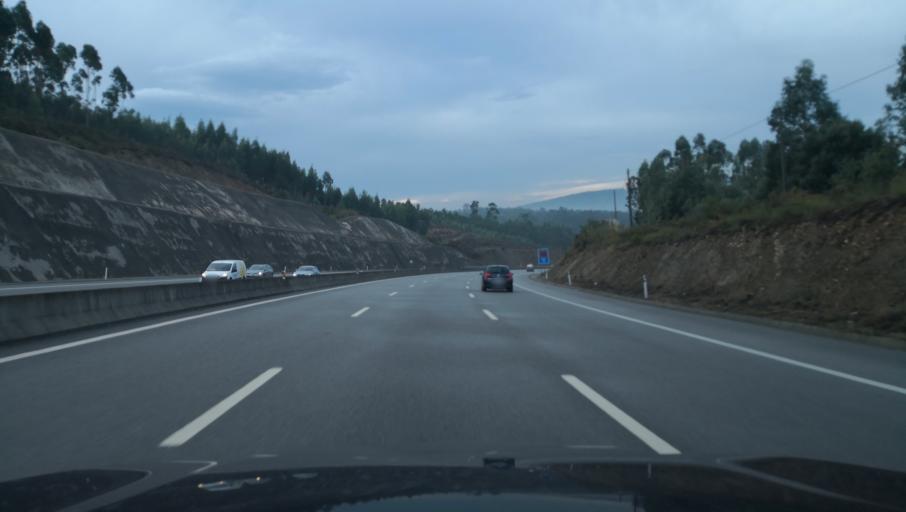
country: PT
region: Porto
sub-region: Paredes
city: Recarei
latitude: 41.1135
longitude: -8.4320
